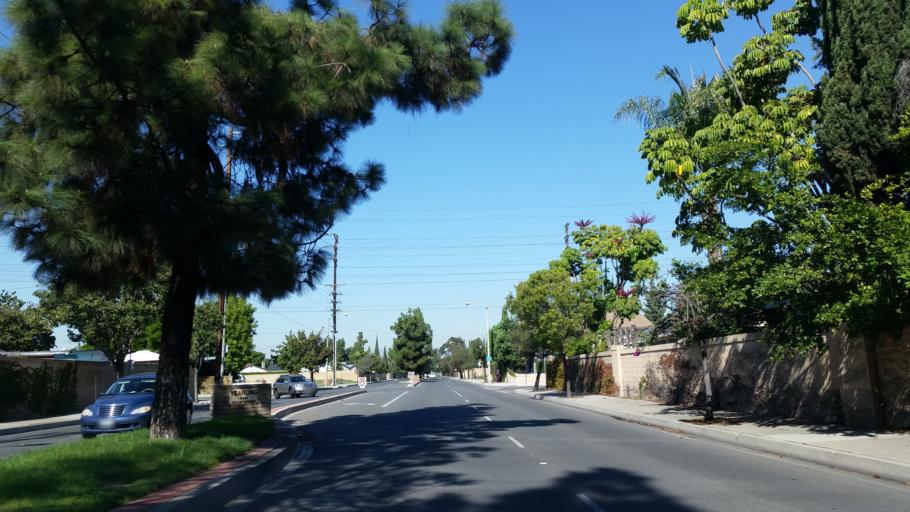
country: US
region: California
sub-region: Los Angeles County
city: Cerritos
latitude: 33.8487
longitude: -118.0721
